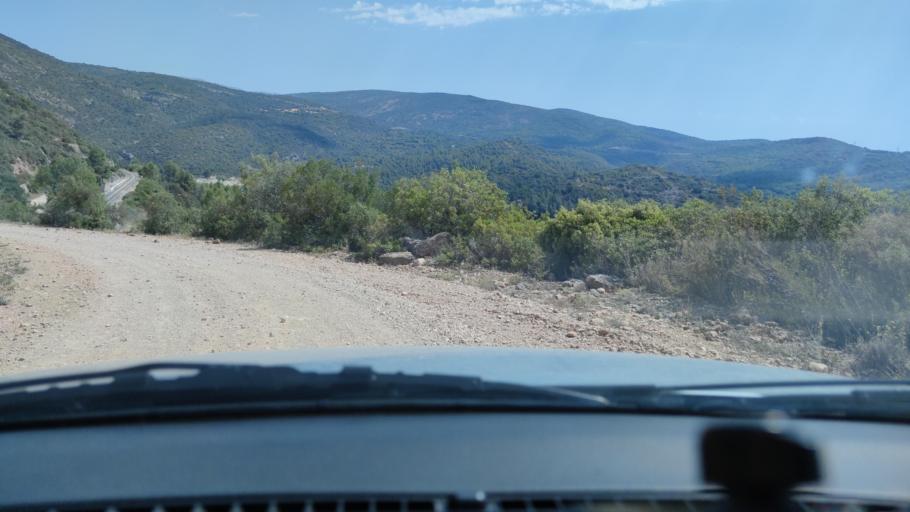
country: ES
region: Catalonia
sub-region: Provincia de Lleida
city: Camarasa
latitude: 41.9296
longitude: 0.8508
